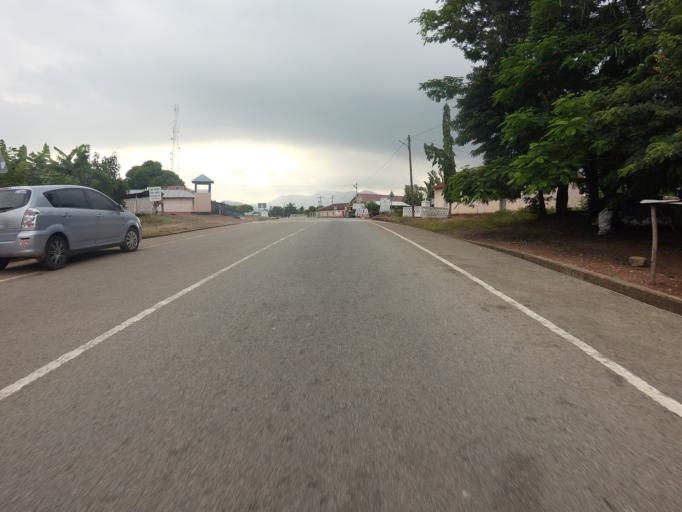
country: GH
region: Volta
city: Ho
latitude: 6.7724
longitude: 0.4796
